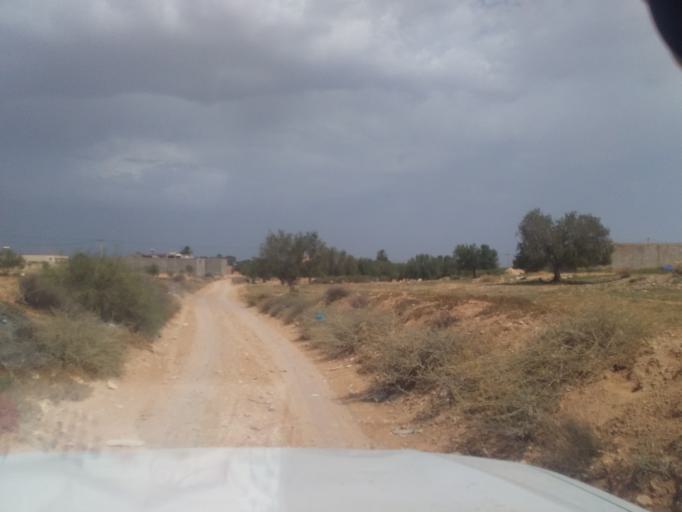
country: TN
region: Madanin
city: Medenine
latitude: 33.5899
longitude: 10.3249
